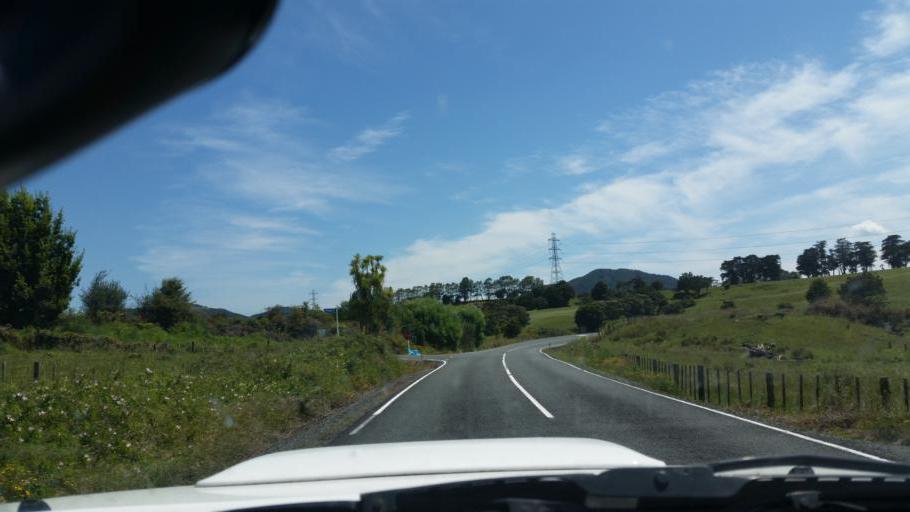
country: NZ
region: Auckland
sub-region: Auckland
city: Wellsford
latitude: -36.1663
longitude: 174.4229
